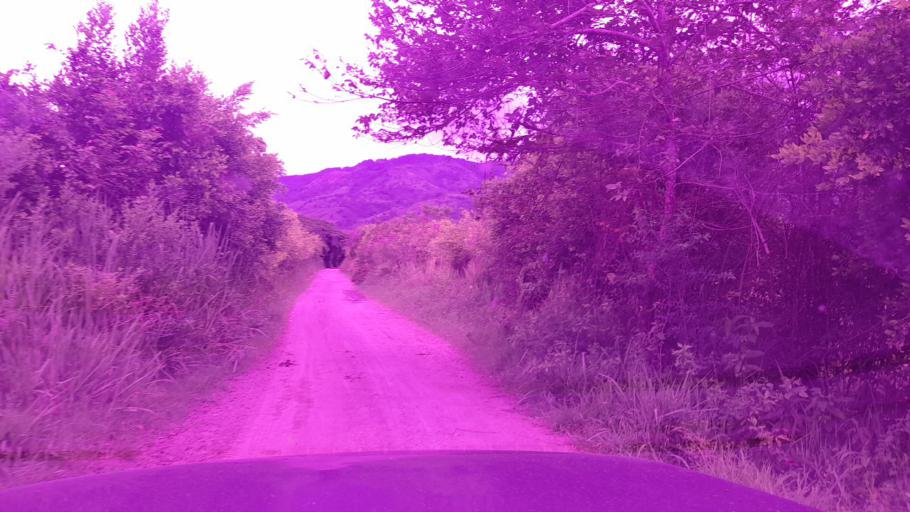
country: CO
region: Valle del Cauca
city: Bugalagrande
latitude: 4.1704
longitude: -76.0776
